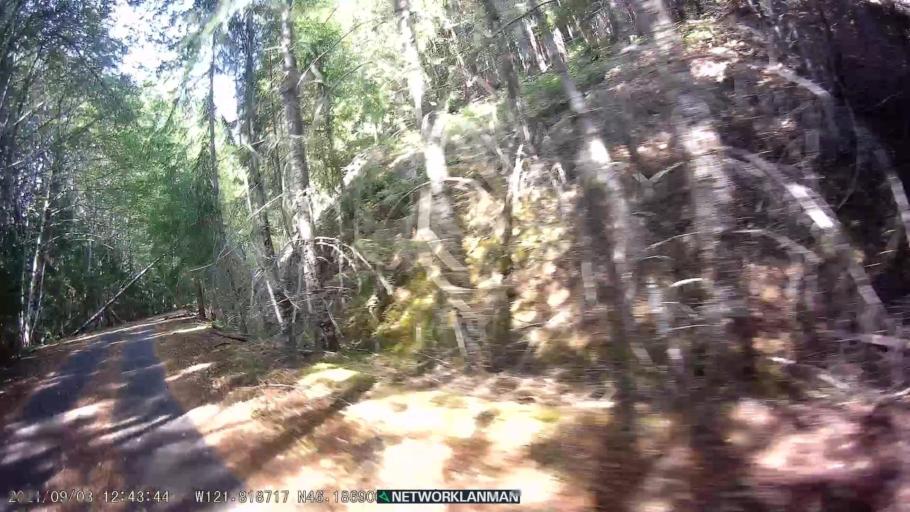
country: US
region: Washington
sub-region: Skamania County
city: Carson
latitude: 46.1869
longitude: -121.8188
